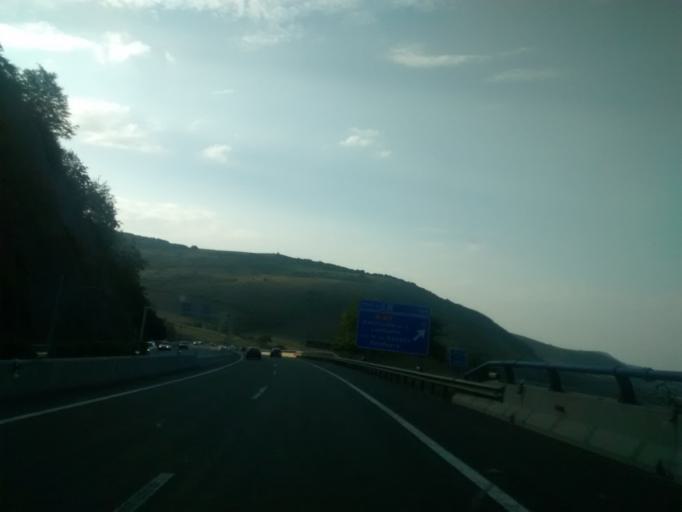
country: ES
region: Cantabria
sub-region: Provincia de Cantabria
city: Santiurde de Reinosa
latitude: 43.0558
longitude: -4.0873
